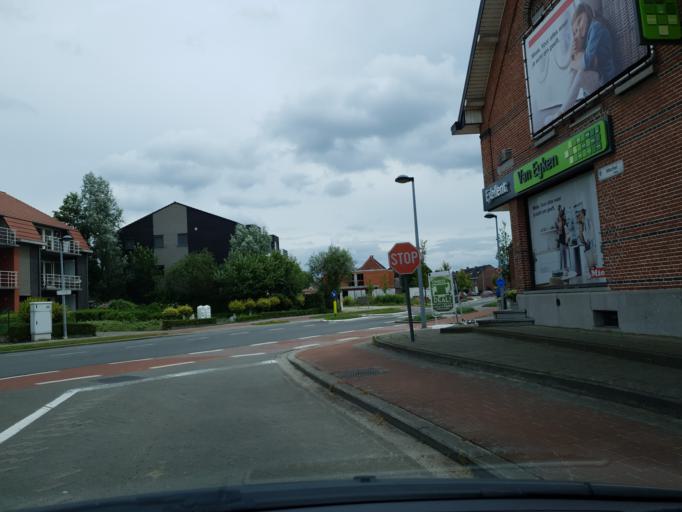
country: BE
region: Flanders
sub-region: Provincie Antwerpen
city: Hulshout
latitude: 51.0524
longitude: 4.7661
